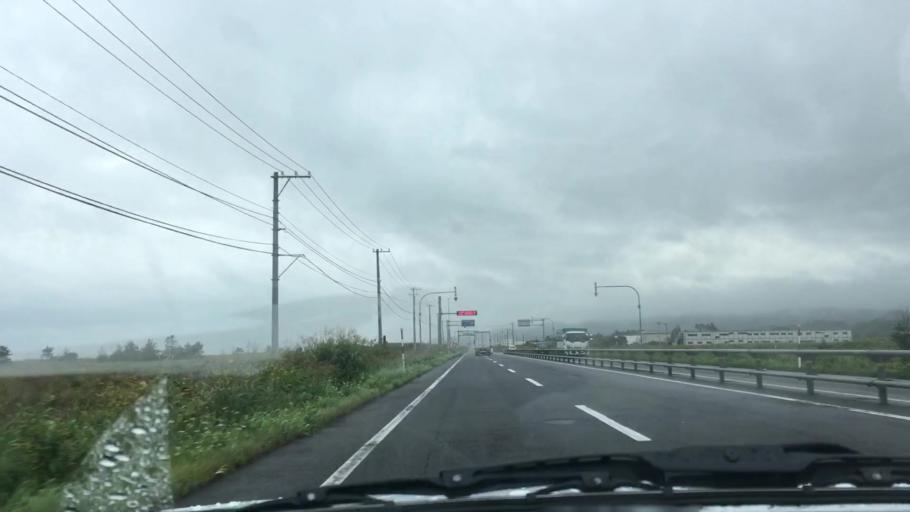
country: JP
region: Hokkaido
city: Niseko Town
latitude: 42.3989
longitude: 140.3023
